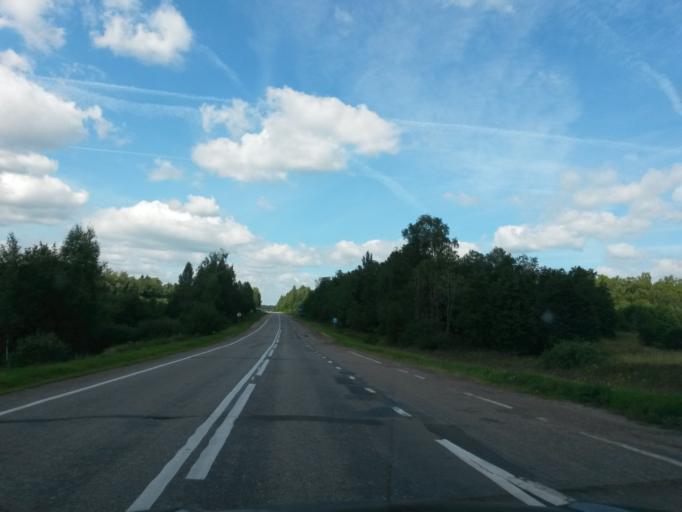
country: RU
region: Jaroslavl
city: Gavrilov-Yam
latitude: 57.4488
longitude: 39.9141
